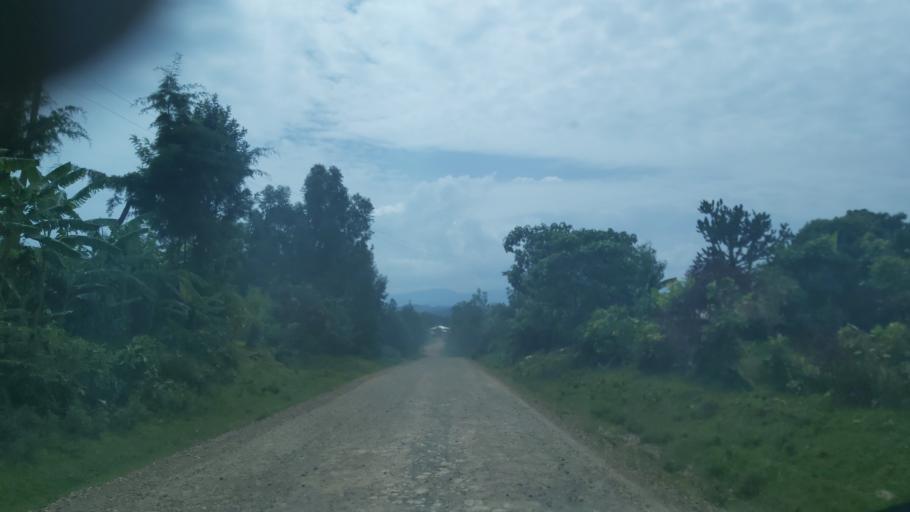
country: ET
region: Oromiya
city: Jima
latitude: 7.7387
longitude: 36.7729
